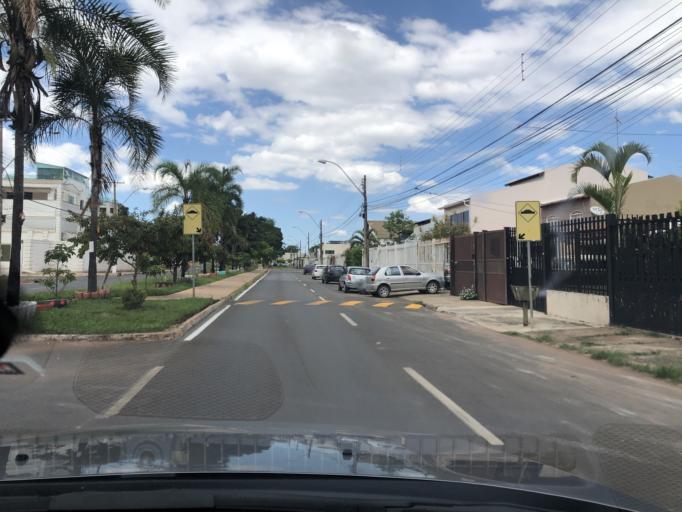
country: BR
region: Federal District
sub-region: Brasilia
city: Brasilia
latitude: -15.9943
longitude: -47.9946
